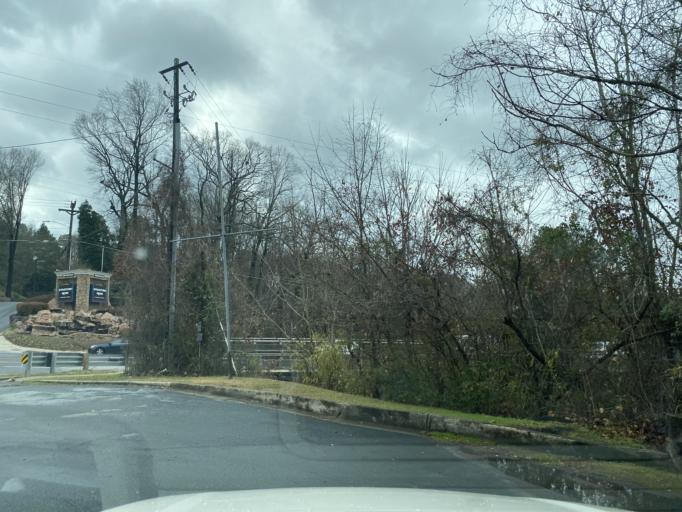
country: US
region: Georgia
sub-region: Cobb County
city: Smyrna
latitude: 33.9231
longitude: -84.4785
